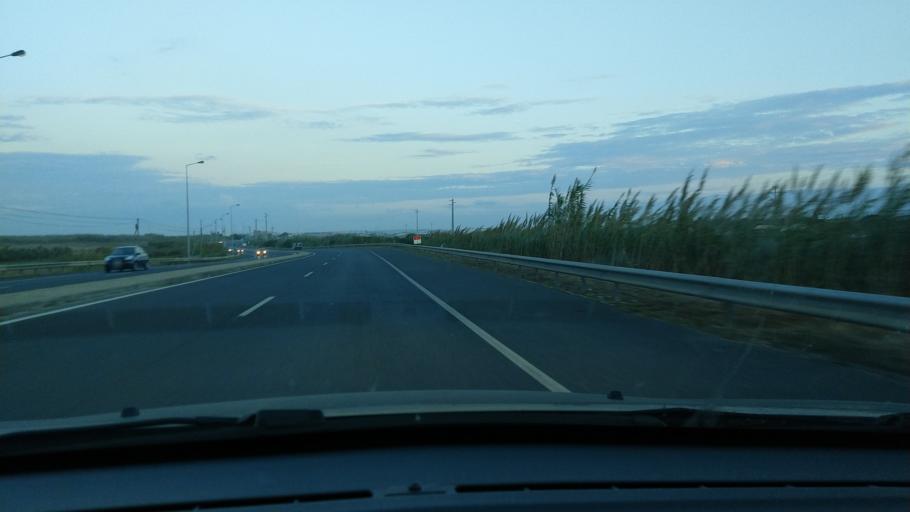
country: PT
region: Leiria
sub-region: Peniche
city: Atouguia da Baleia
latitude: 39.3482
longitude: -9.3499
